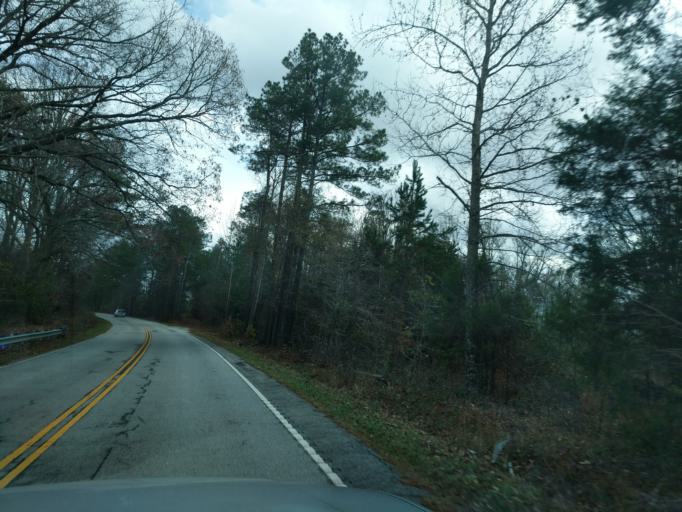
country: US
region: South Carolina
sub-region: Greenwood County
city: Ware Shoals
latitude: 34.3863
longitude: -82.1828
